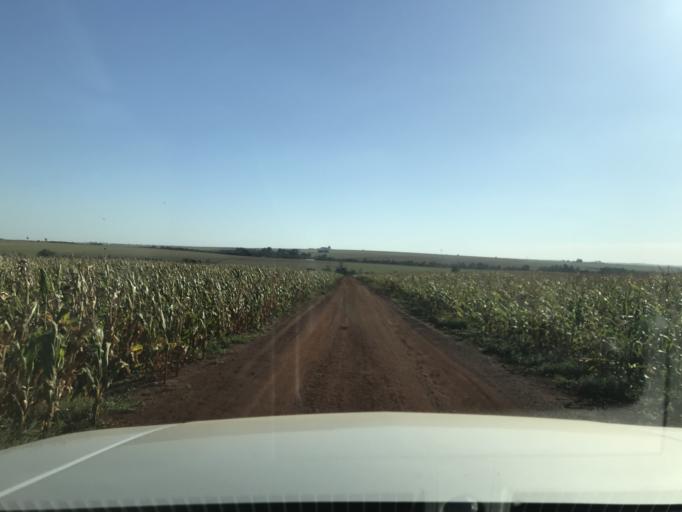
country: BR
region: Parana
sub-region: Palotina
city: Palotina
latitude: -24.2274
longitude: -53.8064
